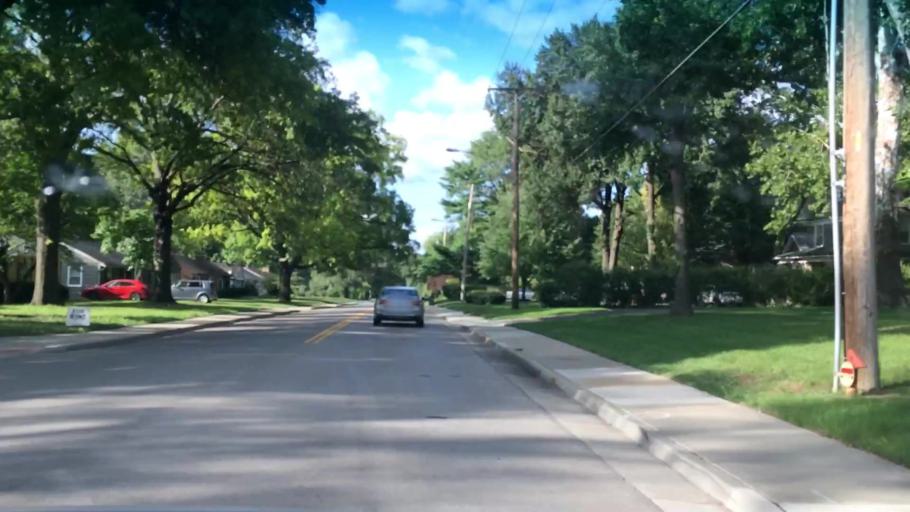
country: US
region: Kansas
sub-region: Johnson County
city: Fairway
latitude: 39.0223
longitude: -94.6303
